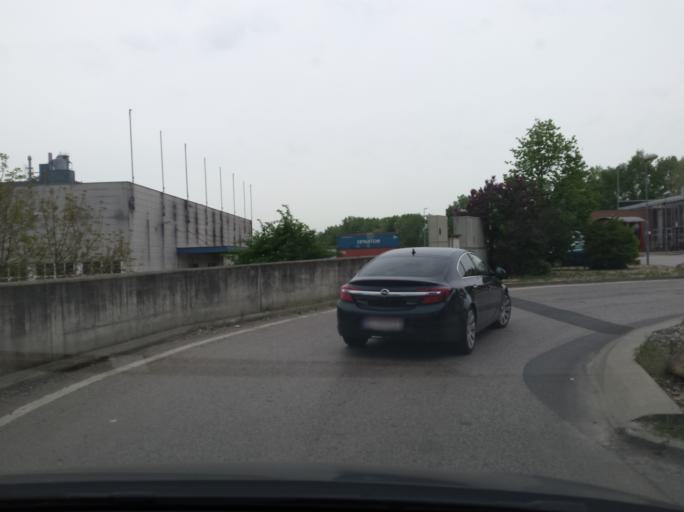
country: AT
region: Lower Austria
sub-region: Politischer Bezirk Wien-Umgebung
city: Schwechat
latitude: 48.1815
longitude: 16.4442
